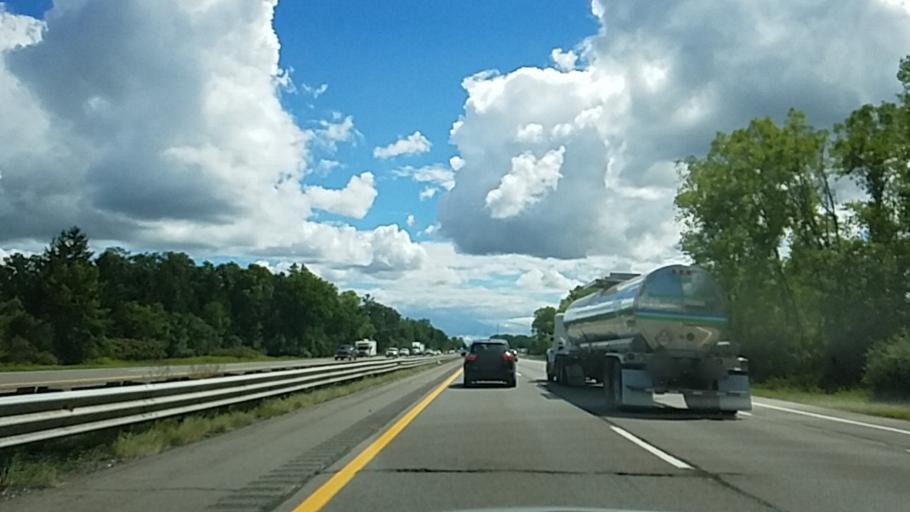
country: US
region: Michigan
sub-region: Livingston County
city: Whitmore Lake
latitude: 42.3611
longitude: -83.7490
